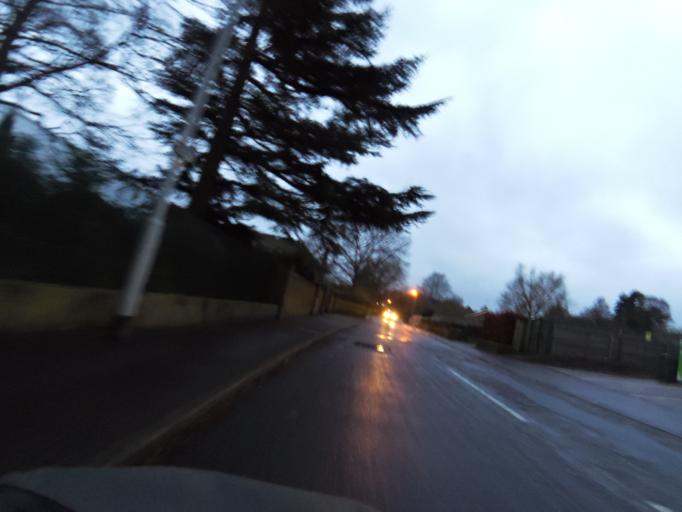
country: GB
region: England
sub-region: Norfolk
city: Costessey
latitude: 52.6759
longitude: 1.2235
